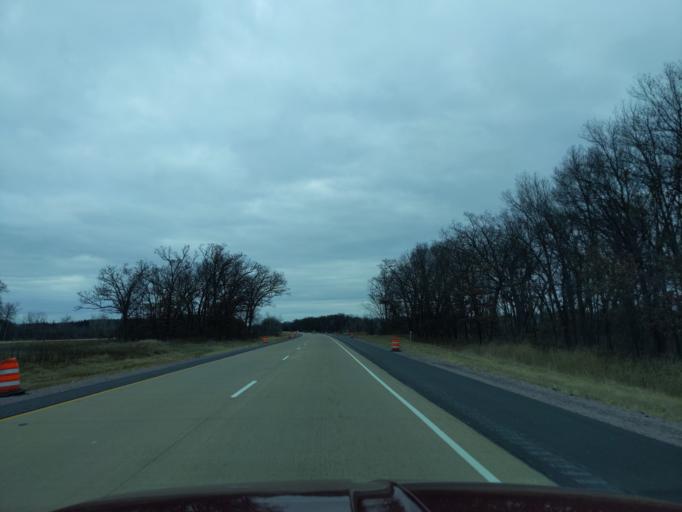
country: US
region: Wisconsin
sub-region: Columbia County
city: Portage
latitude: 43.6304
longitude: -89.4708
